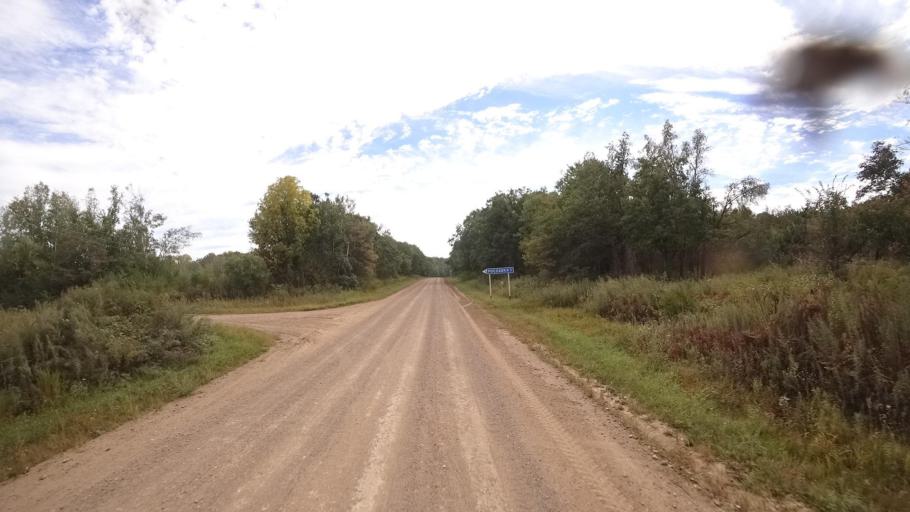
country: RU
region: Primorskiy
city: Yakovlevka
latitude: 44.5152
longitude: 133.5977
